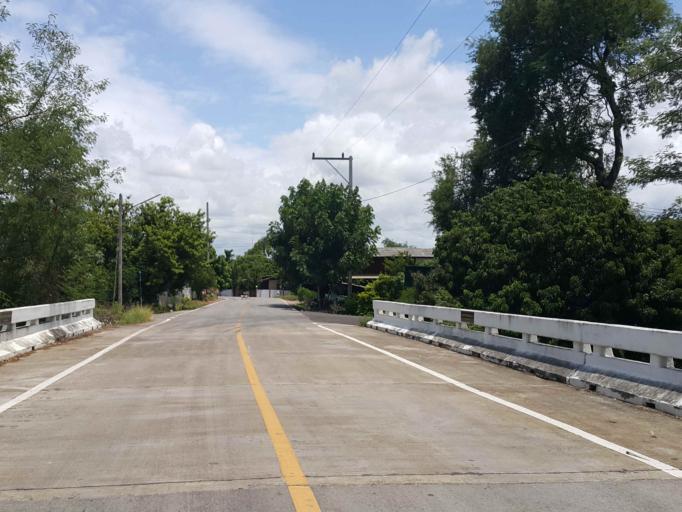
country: TH
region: Lamphun
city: Pa Sang
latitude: 18.5173
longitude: 98.8721
